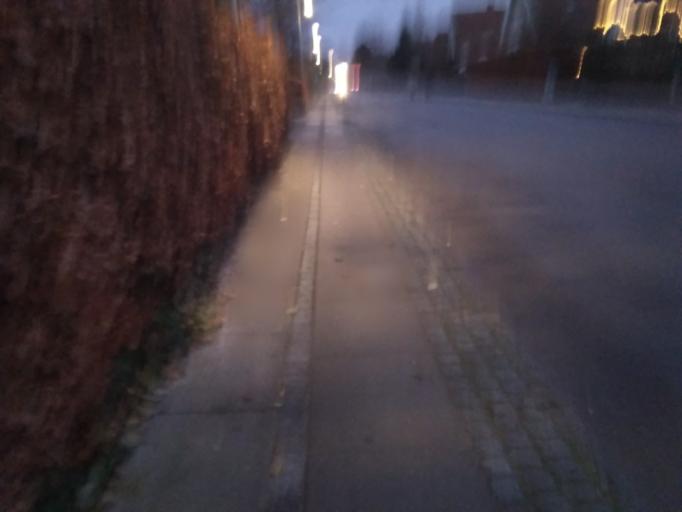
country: DK
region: Capital Region
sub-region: Glostrup Kommune
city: Glostrup
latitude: 55.6705
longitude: 12.3956
